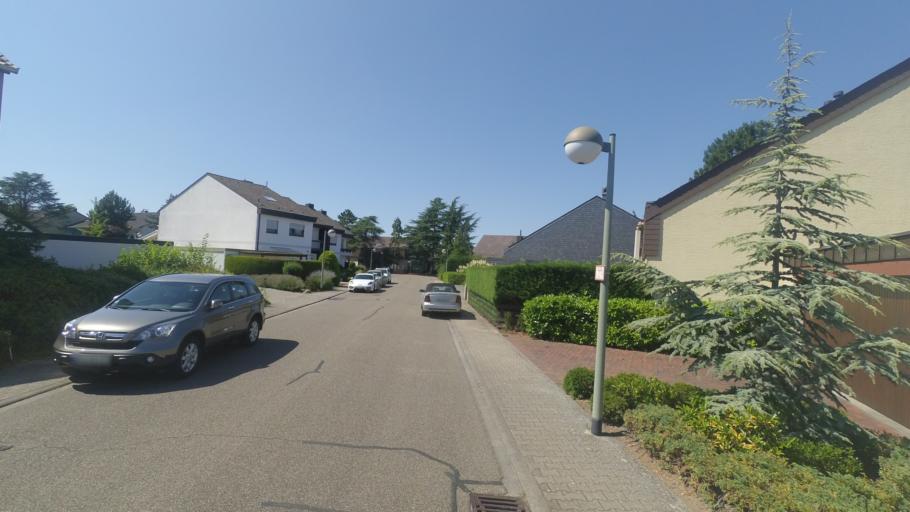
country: DE
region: Rheinland-Pfalz
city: Limburgerhof
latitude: 49.4235
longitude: 8.4012
